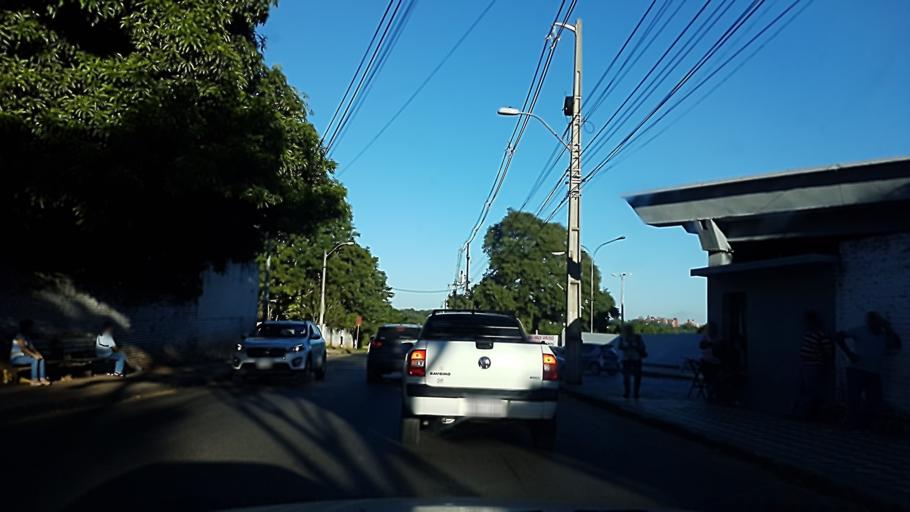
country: PY
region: Asuncion
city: Asuncion
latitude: -25.2733
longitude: -57.5818
